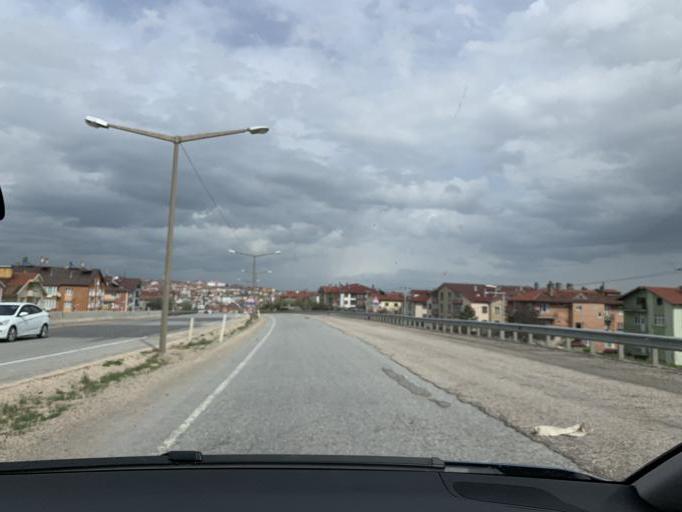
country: TR
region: Bolu
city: Gerede
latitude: 40.7962
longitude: 32.1939
